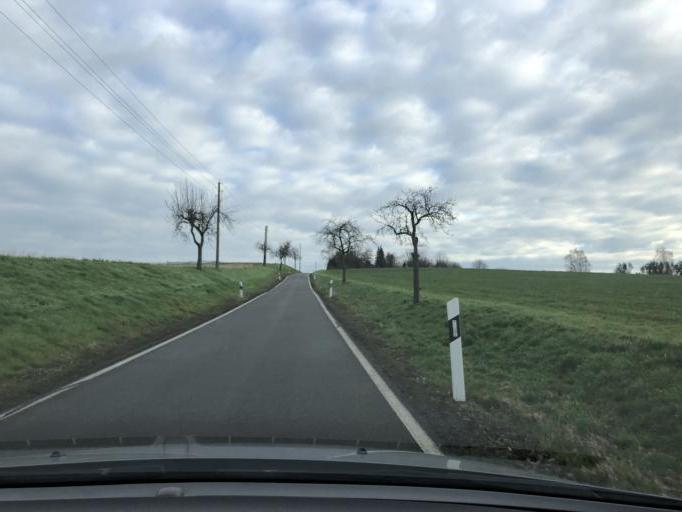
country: DE
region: Saxony
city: Zschadrass
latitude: 51.1986
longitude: 12.8156
